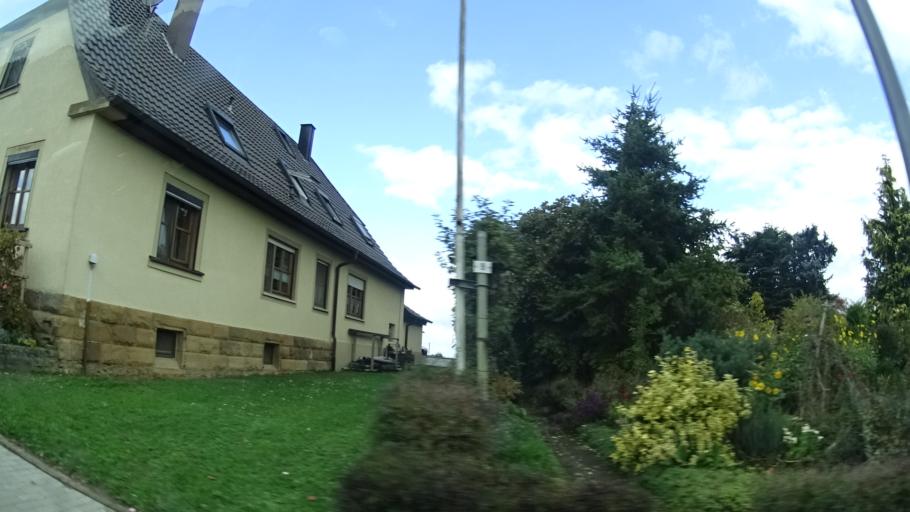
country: DE
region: Bavaria
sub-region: Regierungsbezirk Unterfranken
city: Lulsfeld
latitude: 49.8678
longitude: 10.3270
